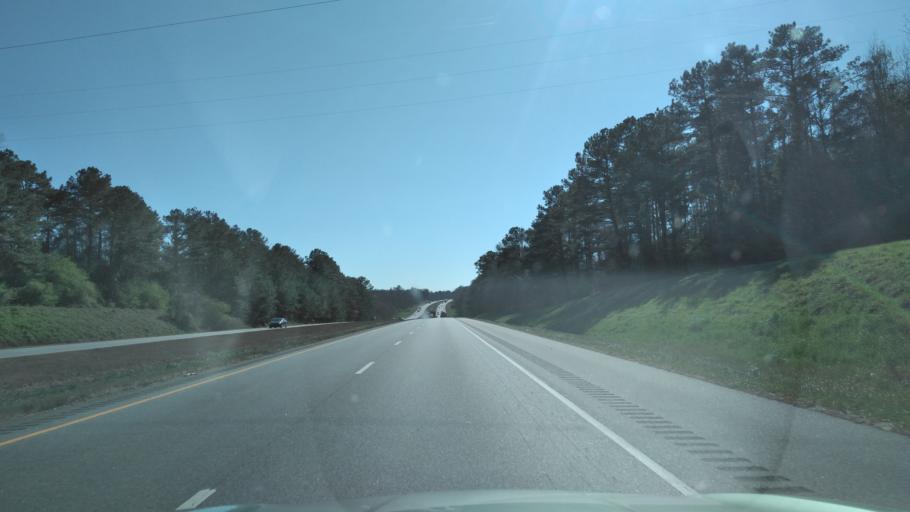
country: US
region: Alabama
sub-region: Lowndes County
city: Fort Deposit
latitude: 31.9238
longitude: -86.5764
